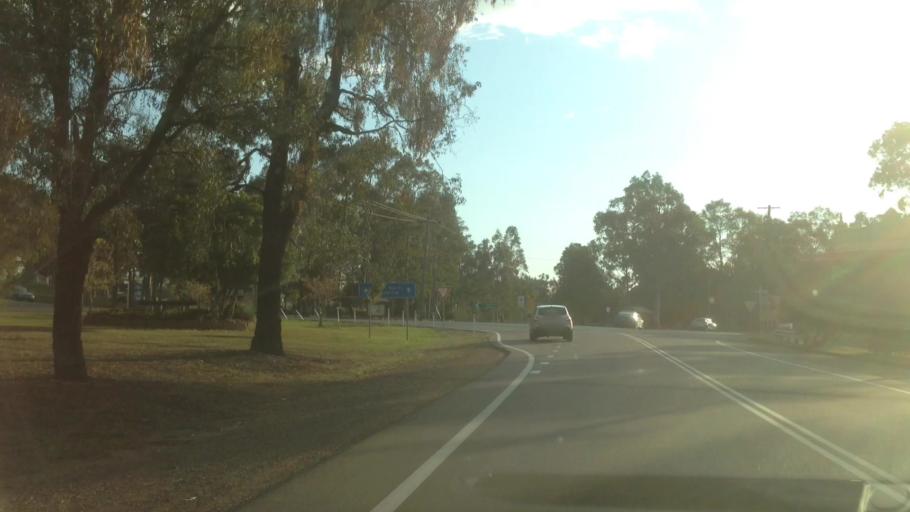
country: AU
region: New South Wales
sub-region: Cessnock
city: Kurri Kurri
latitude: -32.8252
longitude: 151.4835
